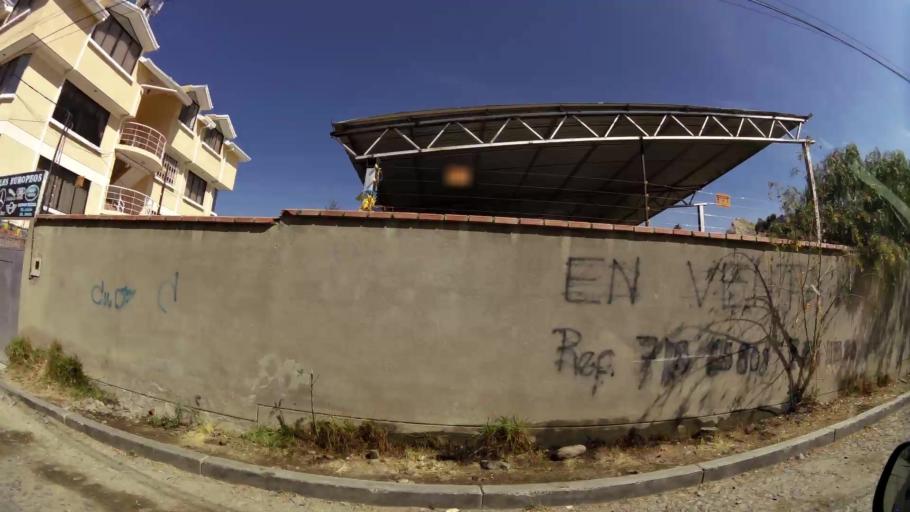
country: BO
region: La Paz
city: La Paz
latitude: -16.5230
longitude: -68.0884
